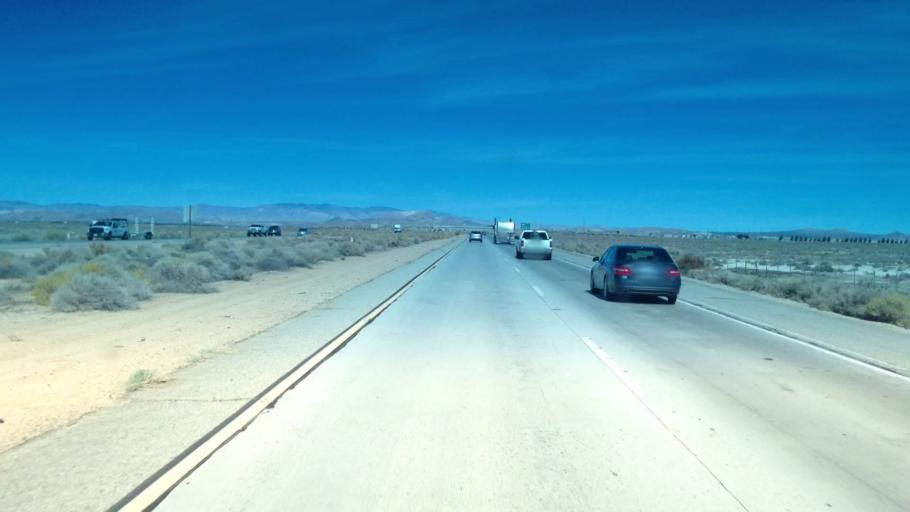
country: US
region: California
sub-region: Los Angeles County
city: Lancaster
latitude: 34.7656
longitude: -118.1704
